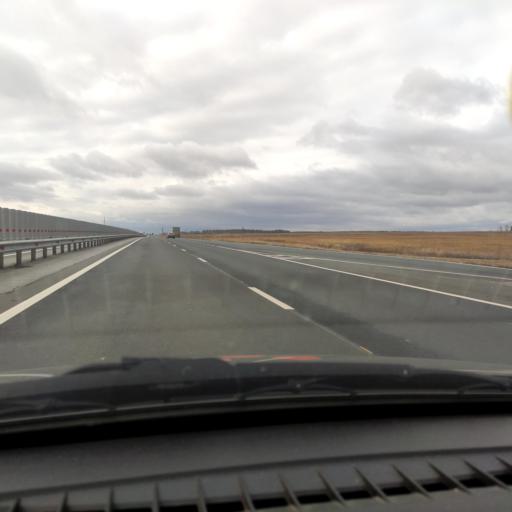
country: RU
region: Samara
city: Bereza
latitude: 53.4686
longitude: 50.1808
